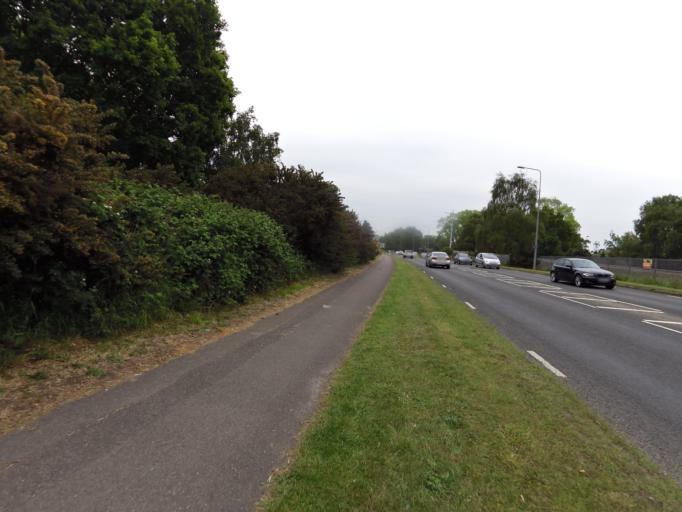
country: GB
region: England
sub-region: Suffolk
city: Kesgrave
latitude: 52.0370
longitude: 1.2033
